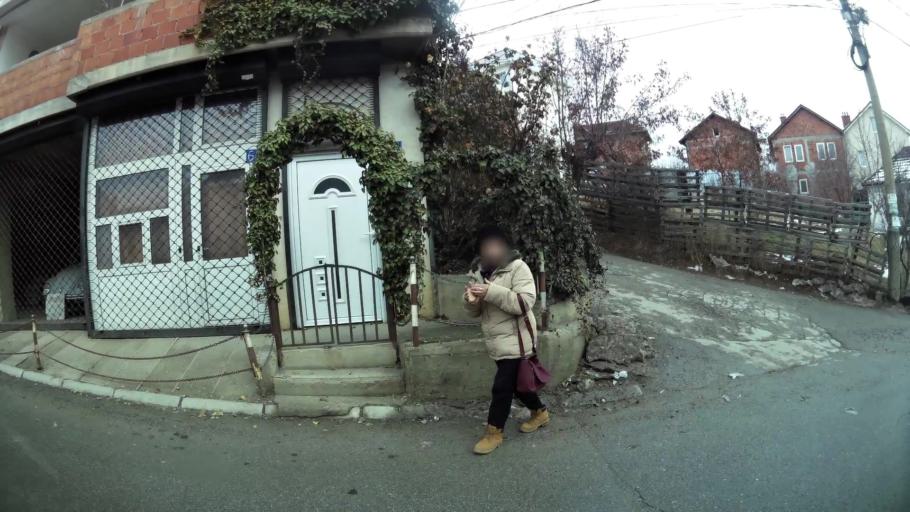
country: XK
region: Pristina
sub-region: Komuna e Prishtines
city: Pristina
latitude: 42.6802
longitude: 21.1656
